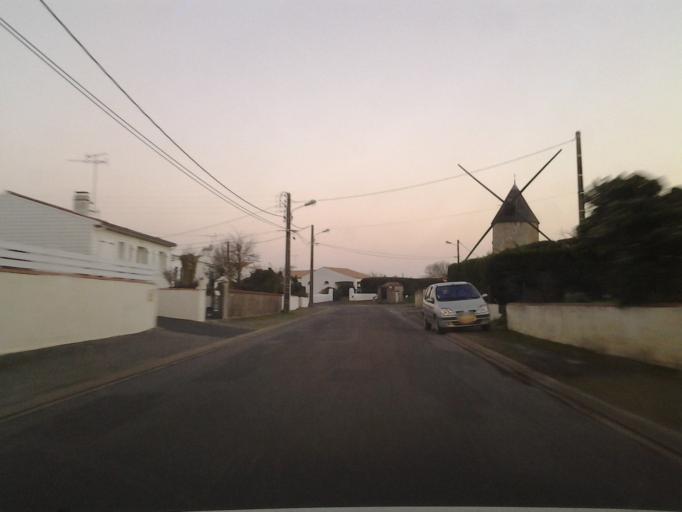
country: FR
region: Pays de la Loire
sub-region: Departement de la Vendee
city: Beauvoir-sur-Mer
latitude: 46.9104
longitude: -2.0384
